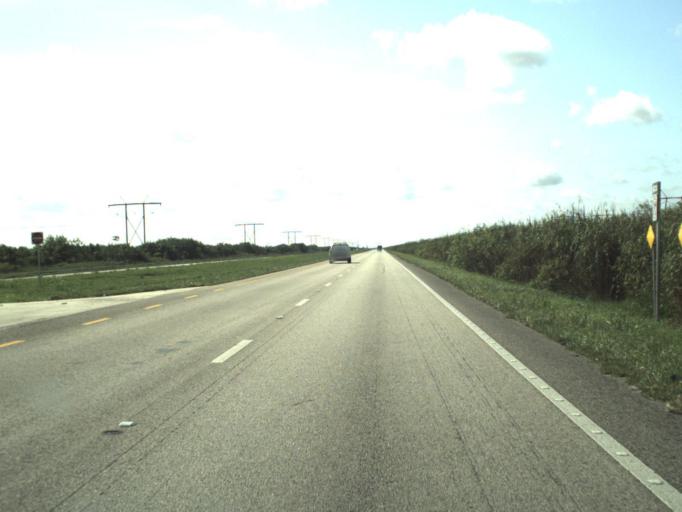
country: US
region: Florida
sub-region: Broward County
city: Weston
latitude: 26.2696
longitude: -80.4876
